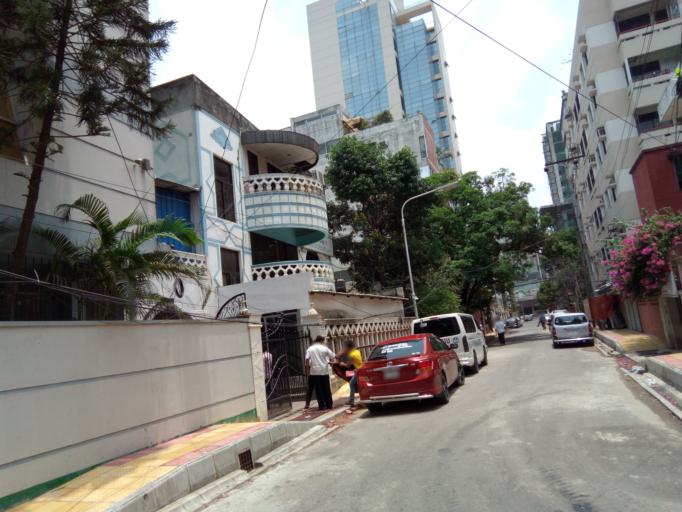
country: BD
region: Dhaka
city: Paltan
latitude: 23.7896
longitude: 90.4016
